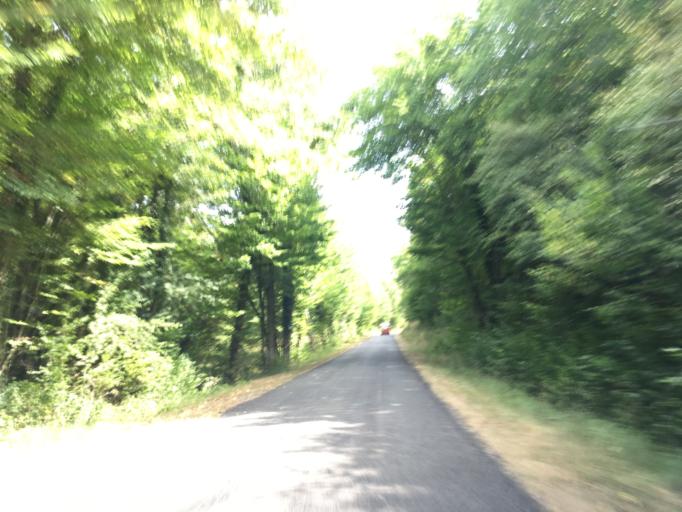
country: FR
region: Midi-Pyrenees
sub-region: Departement du Lot
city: Gramat
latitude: 44.7647
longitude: 1.5810
